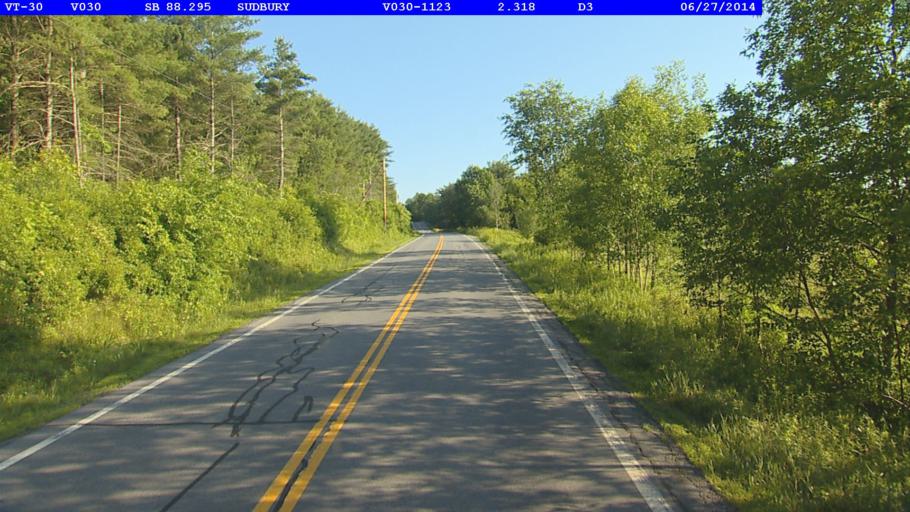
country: US
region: Vermont
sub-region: Rutland County
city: Brandon
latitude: 43.7814
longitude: -73.2032
